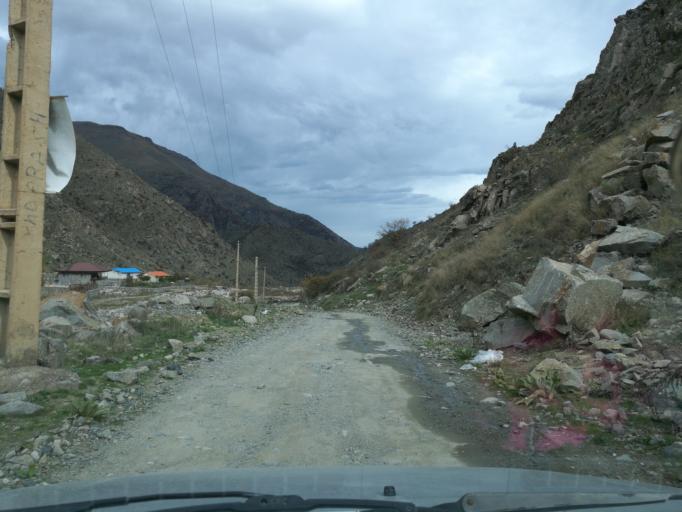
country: IR
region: Mazandaran
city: `Abbasabad
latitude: 36.4273
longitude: 51.0383
